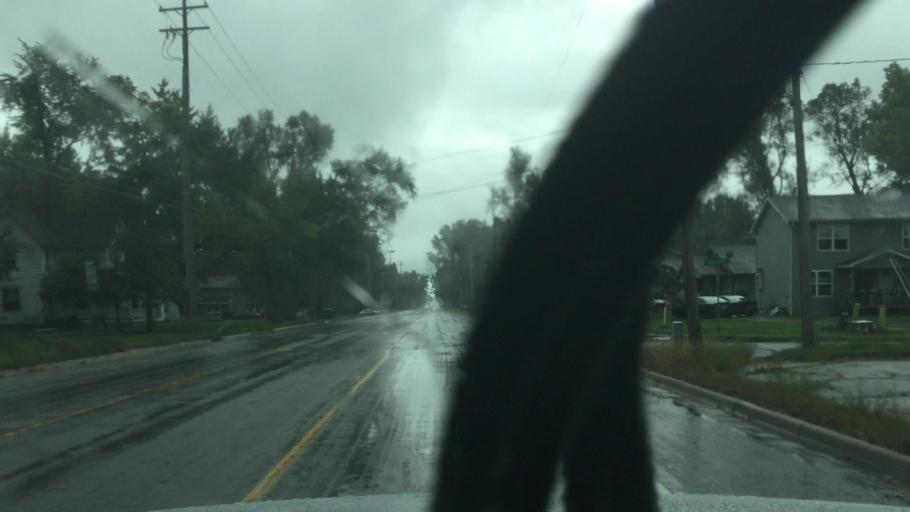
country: US
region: Michigan
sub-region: Eaton County
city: Dimondale
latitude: 42.6808
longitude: -84.6031
